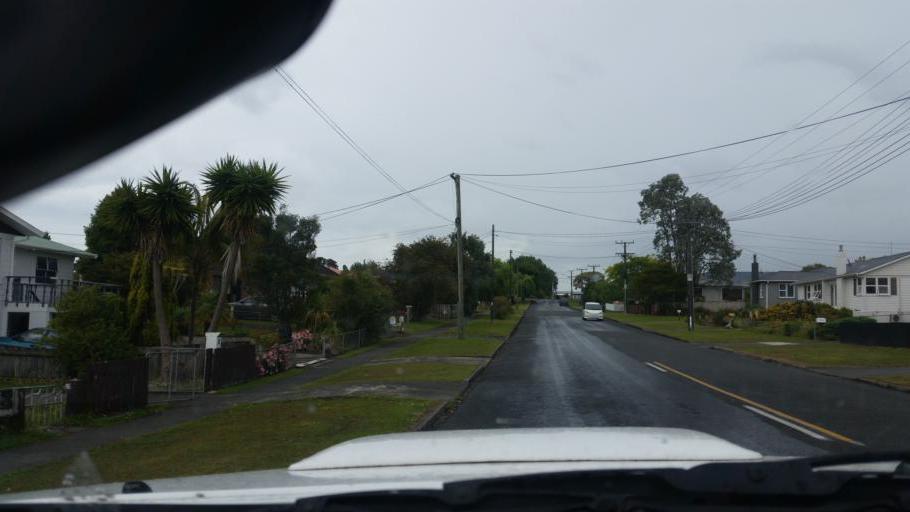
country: NZ
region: Northland
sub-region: Kaipara District
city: Dargaville
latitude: -35.9314
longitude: 173.8608
